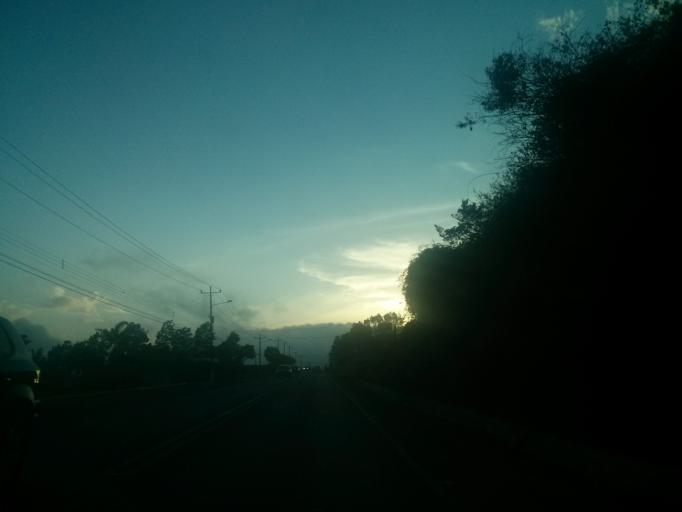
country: CR
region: Cartago
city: Cartago
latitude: 9.8788
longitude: -83.9122
